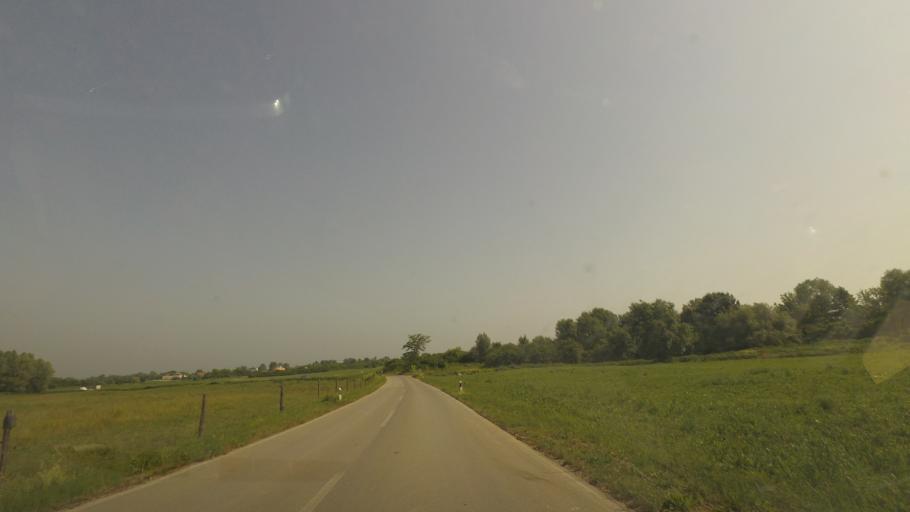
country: HR
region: Karlovacka
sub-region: Grad Karlovac
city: Karlovac
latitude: 45.4845
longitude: 15.5901
